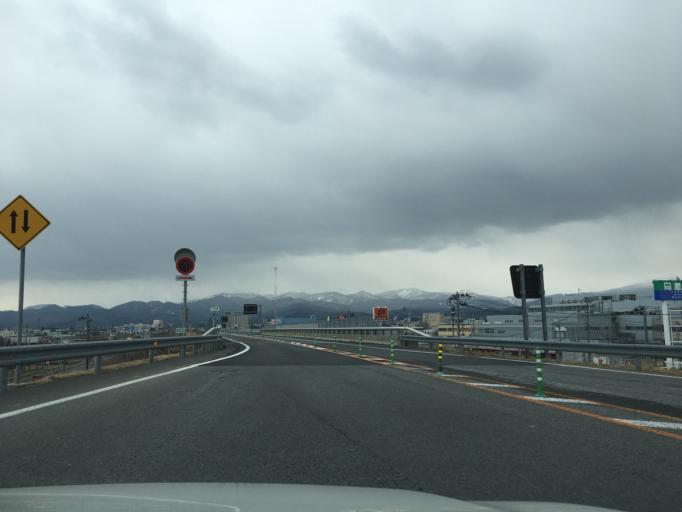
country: JP
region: Aomori
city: Aomori Shi
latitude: 40.7960
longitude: 140.7465
